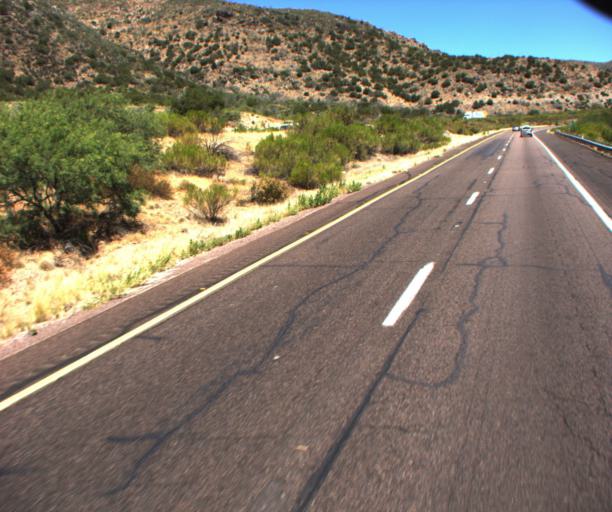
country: US
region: Arizona
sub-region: Gila County
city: Tonto Basin
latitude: 33.9860
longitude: -111.3828
